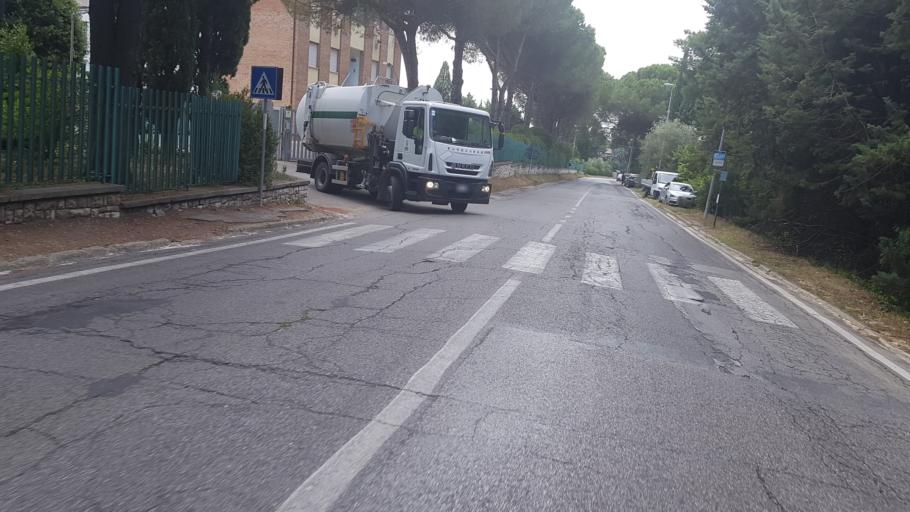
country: IT
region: Umbria
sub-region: Provincia di Perugia
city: Perugia
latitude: 43.0804
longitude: 12.4002
